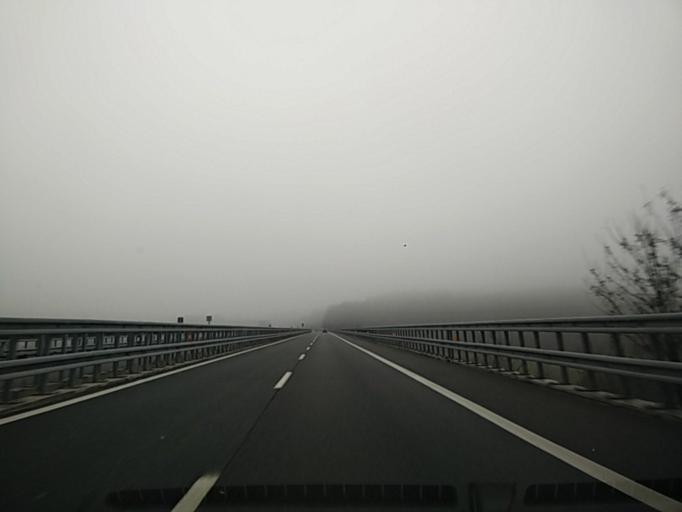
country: IT
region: Piedmont
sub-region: Provincia di Asti
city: San Paolo Solbrito
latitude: 44.9425
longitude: 7.9813
